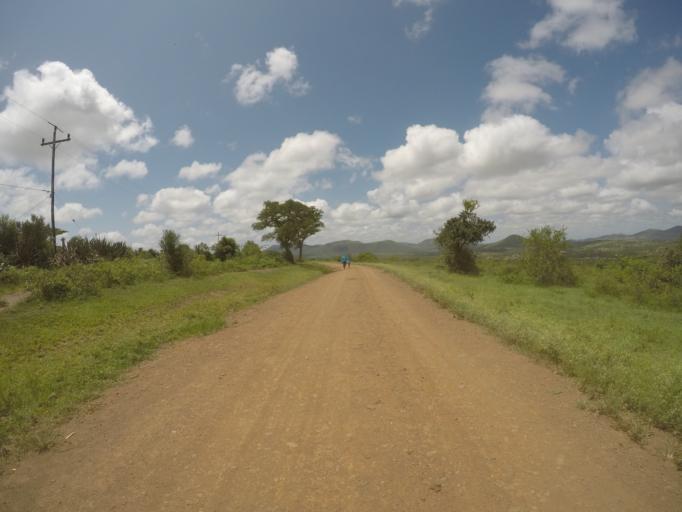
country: ZA
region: KwaZulu-Natal
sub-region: uThungulu District Municipality
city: Empangeni
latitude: -28.5857
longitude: 31.8245
